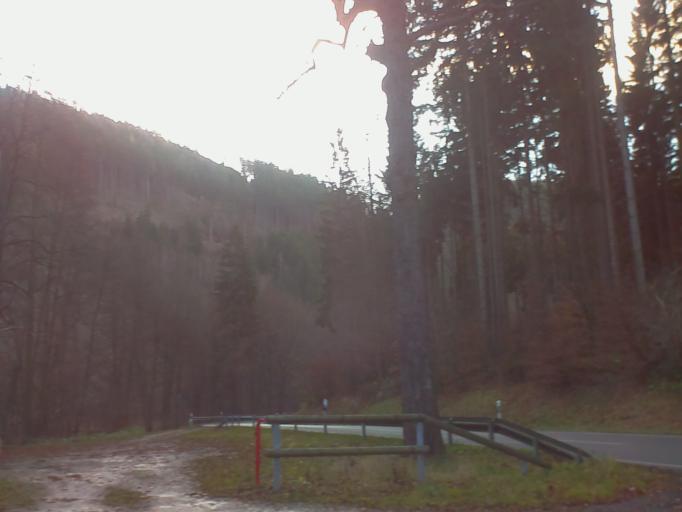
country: DE
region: Thuringia
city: Schwarzburg
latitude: 50.6586
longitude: 11.2157
